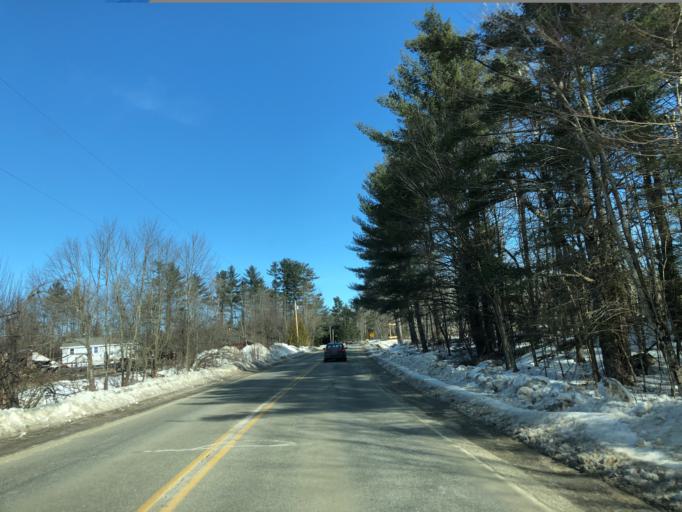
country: US
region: Maine
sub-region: Oxford County
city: Buckfield
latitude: 44.2304
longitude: -70.3385
